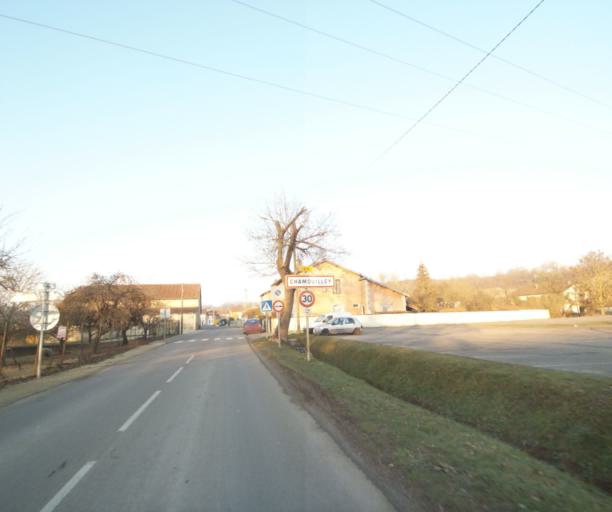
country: FR
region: Champagne-Ardenne
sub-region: Departement de la Haute-Marne
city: Bienville
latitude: 48.6020
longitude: 5.0444
